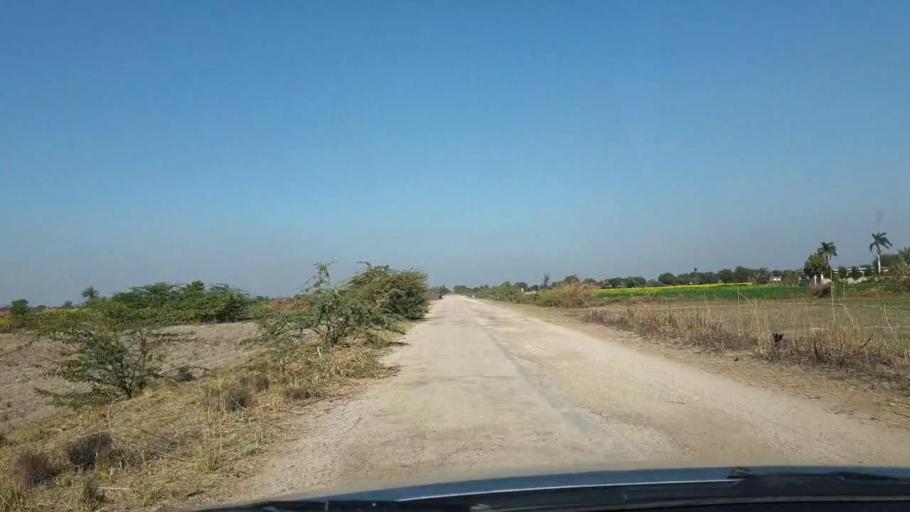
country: PK
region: Sindh
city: Jhol
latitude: 25.9236
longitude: 68.9080
